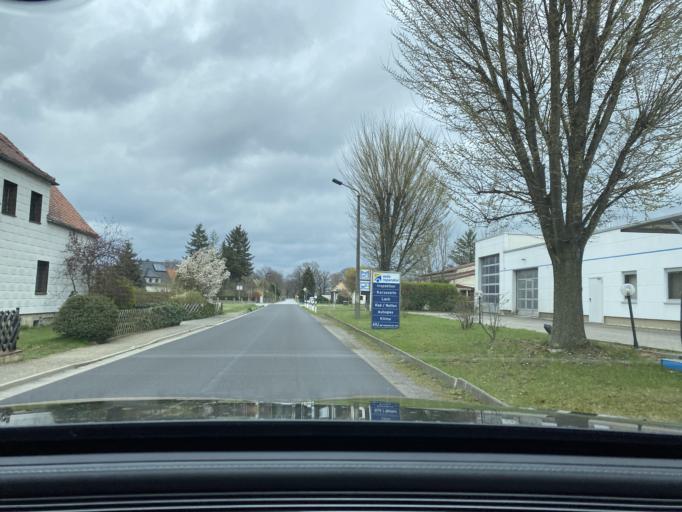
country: DE
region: Saxony
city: Neschwitz
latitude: 51.2669
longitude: 14.3339
